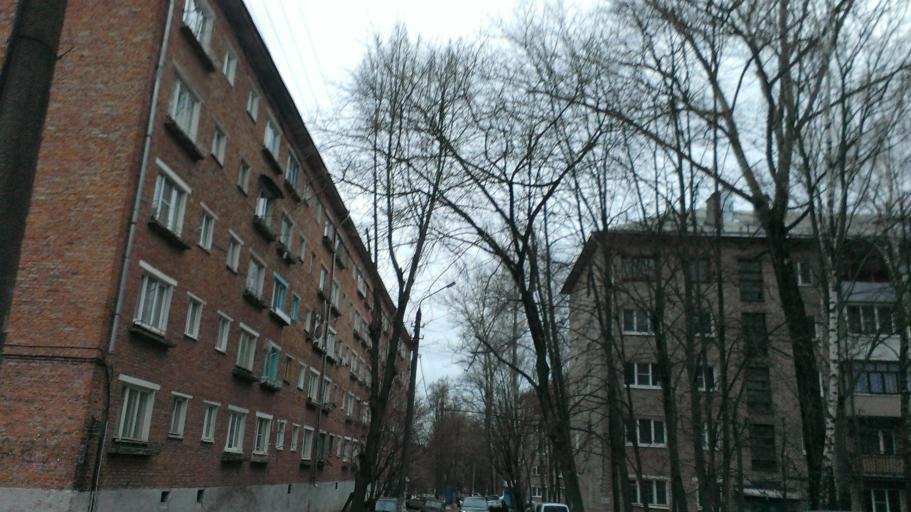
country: RU
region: Tula
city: Tula
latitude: 54.1893
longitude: 37.6934
